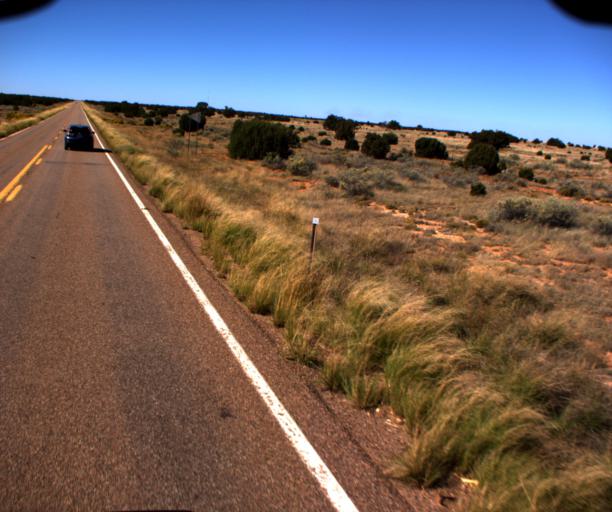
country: US
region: Arizona
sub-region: Navajo County
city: Heber-Overgaard
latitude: 34.4719
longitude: -110.3596
